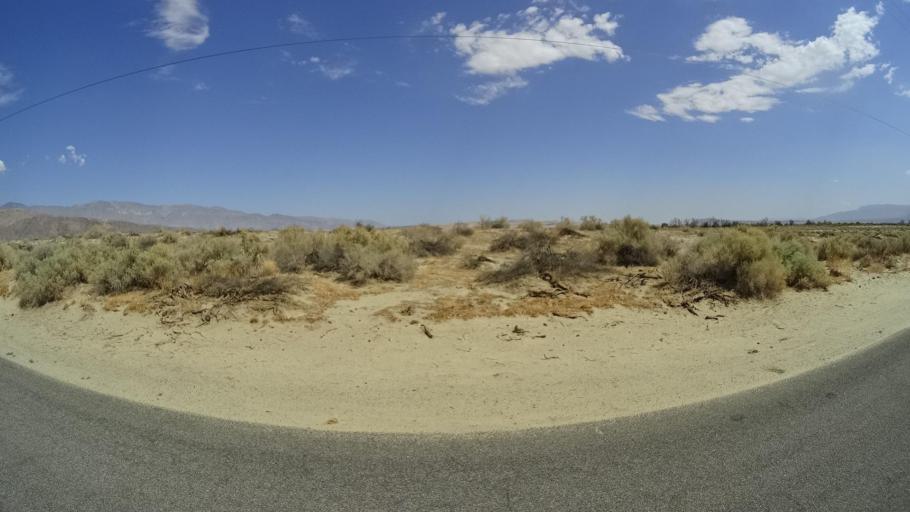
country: US
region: California
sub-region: San Diego County
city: Borrego Springs
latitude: 33.2746
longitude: -116.3486
